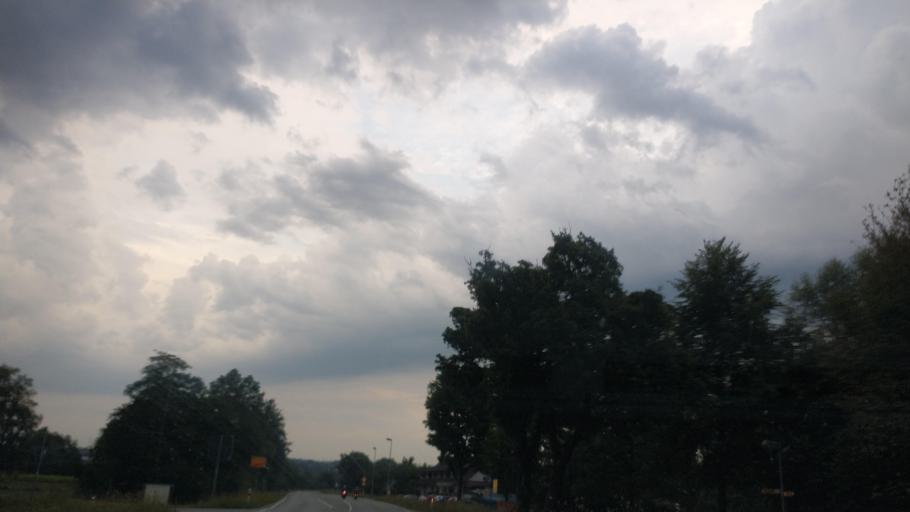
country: DE
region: Baden-Wuerttemberg
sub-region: Tuebingen Region
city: Tettnang
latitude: 47.6681
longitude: 9.5625
